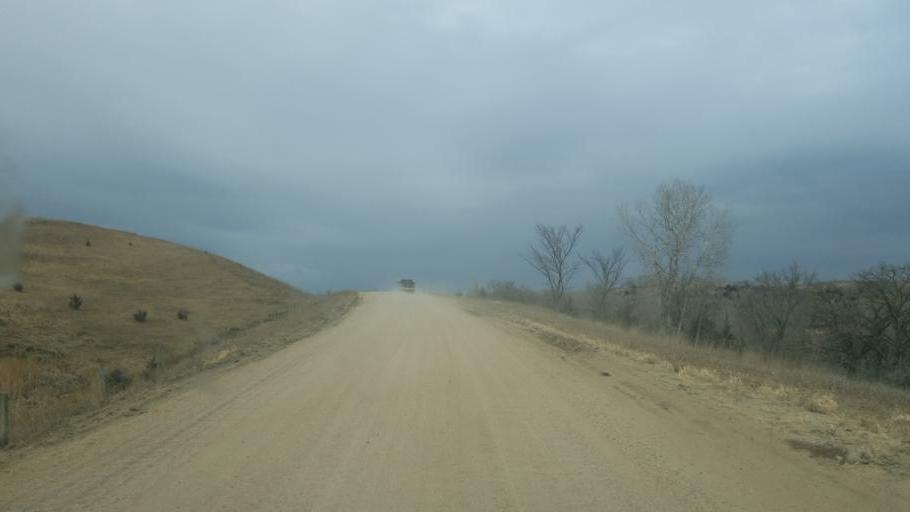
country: US
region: Nebraska
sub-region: Knox County
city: Center
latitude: 42.7100
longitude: -97.9025
